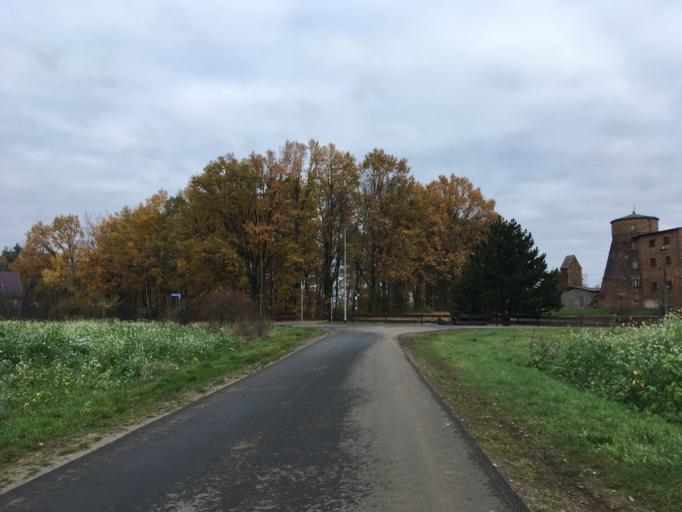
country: DE
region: Brandenburg
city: Drehnow
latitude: 51.8612
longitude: 14.3832
